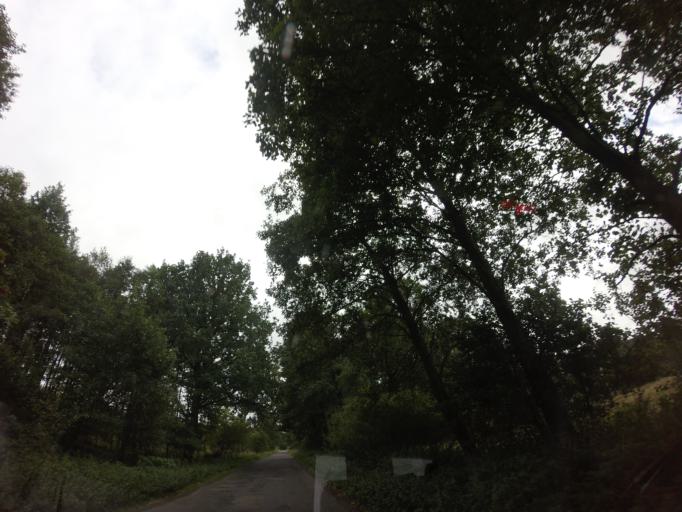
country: PL
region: West Pomeranian Voivodeship
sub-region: Powiat goleniowski
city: Stepnica
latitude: 53.6641
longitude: 14.6641
